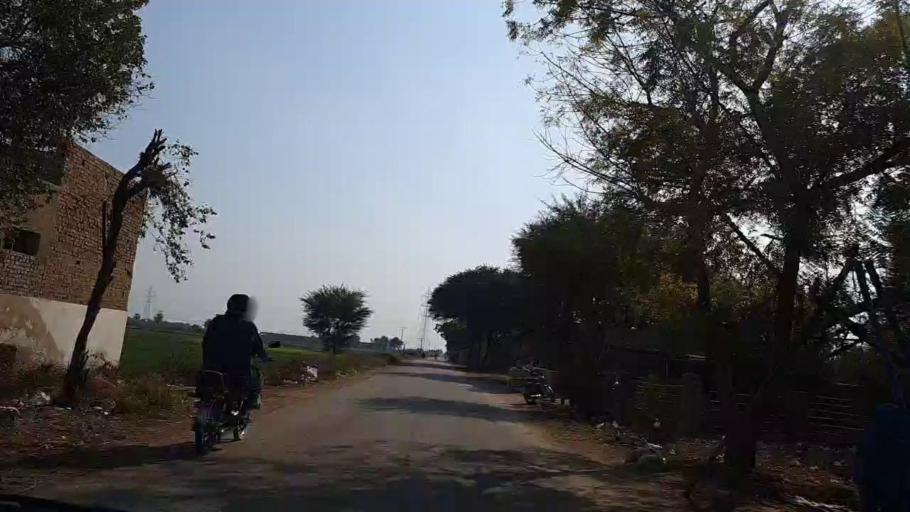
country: PK
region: Sindh
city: Sakrand
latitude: 26.1101
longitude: 68.2909
